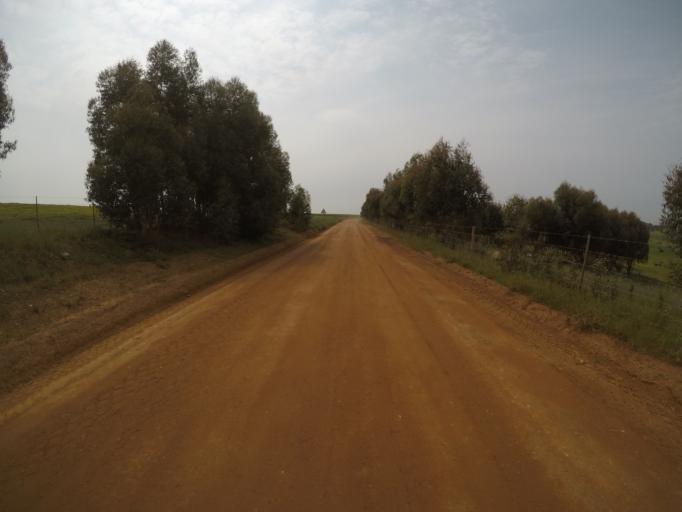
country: ZA
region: Western Cape
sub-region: City of Cape Town
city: Kraaifontein
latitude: -33.7245
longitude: 18.6544
